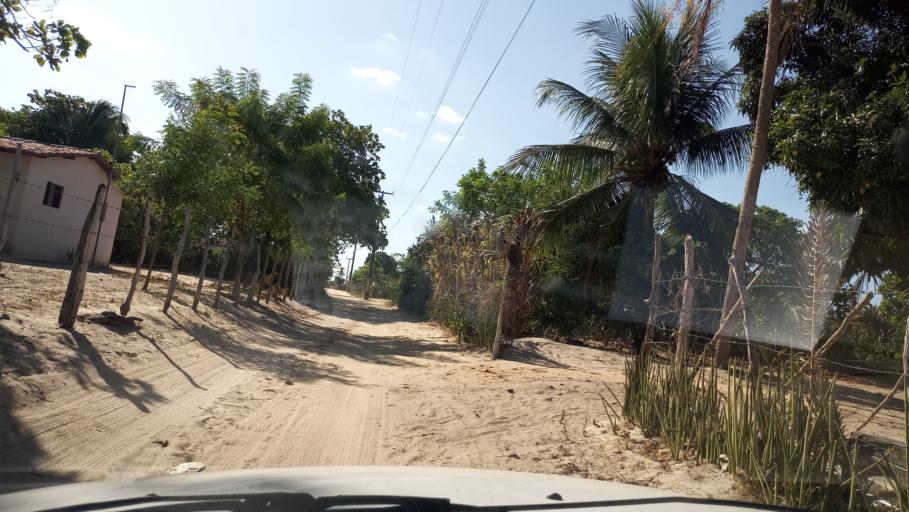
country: BR
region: Rio Grande do Norte
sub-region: Brejinho
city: Brejinho
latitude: -6.1751
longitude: -35.4642
